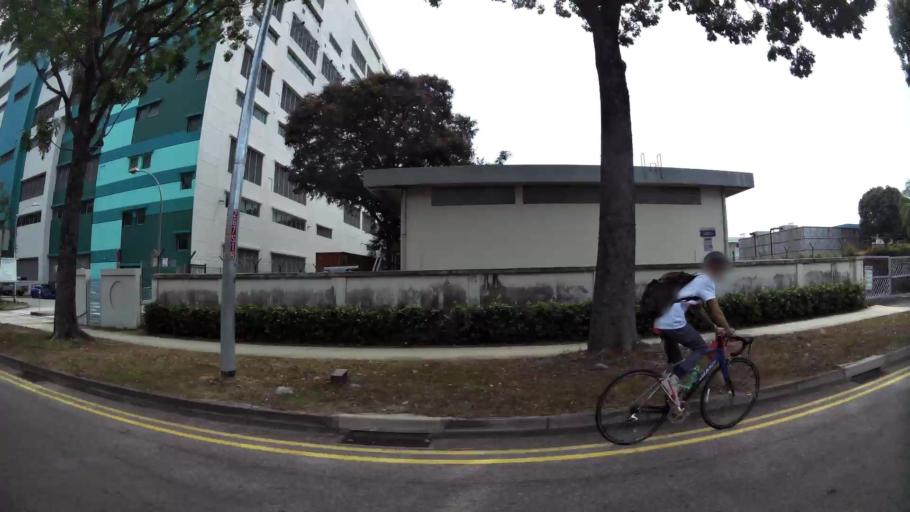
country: MY
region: Johor
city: Johor Bahru
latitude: 1.3224
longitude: 103.6943
